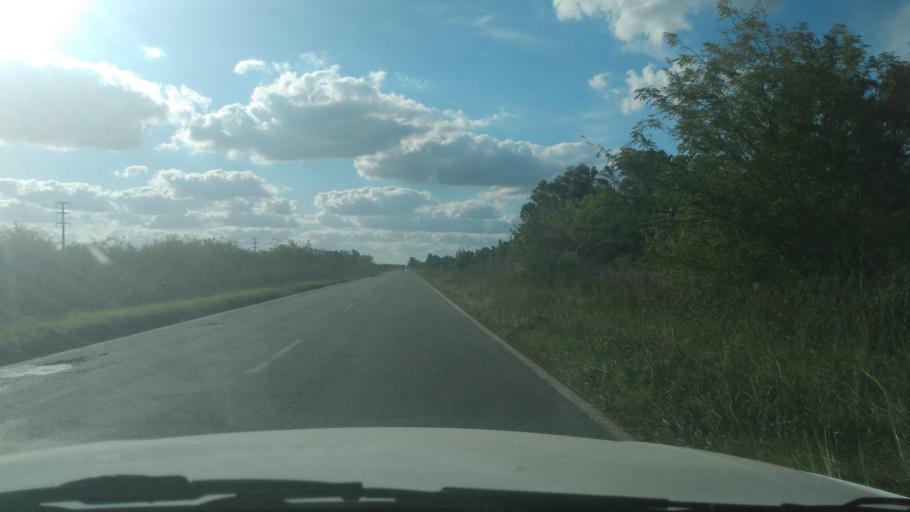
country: AR
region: Buenos Aires
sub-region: Partido de Mercedes
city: Mercedes
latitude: -34.7524
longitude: -59.3798
